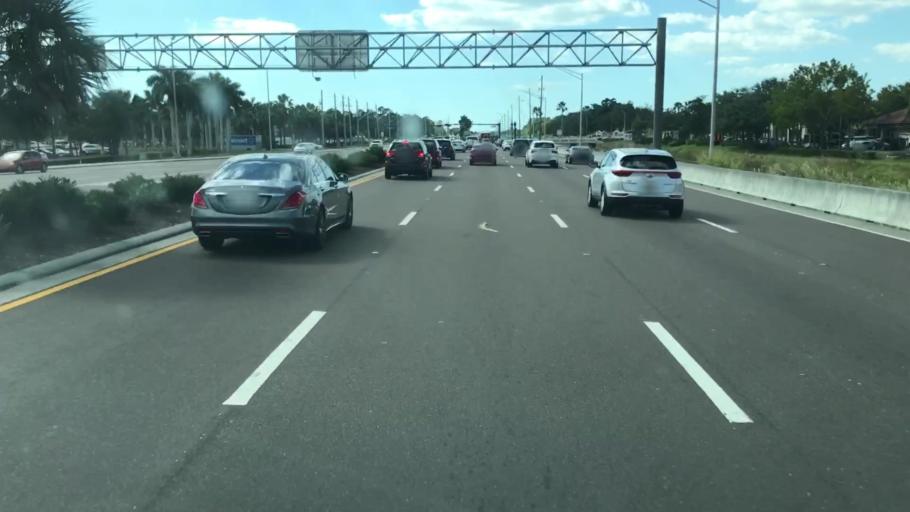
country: US
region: Florida
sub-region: Collier County
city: Vineyards
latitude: 26.2729
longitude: -81.7447
